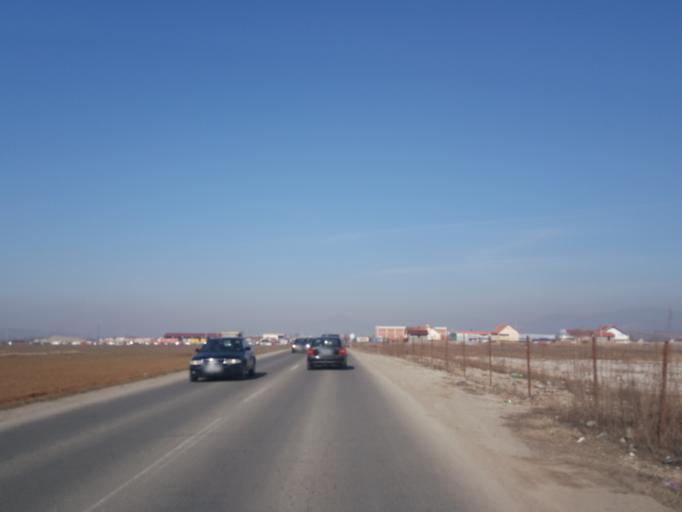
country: XK
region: Mitrovica
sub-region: Vushtrri
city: Vushtrri
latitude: 42.7880
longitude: 21.0071
